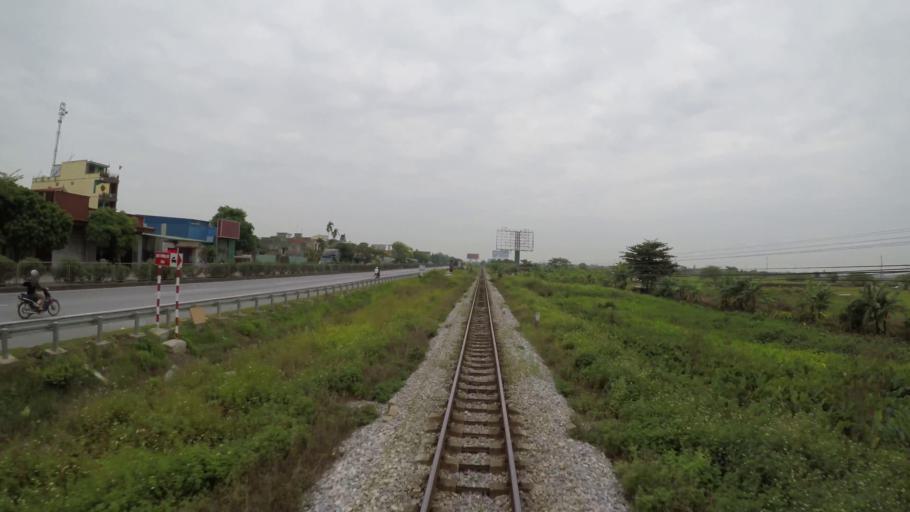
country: VN
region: Hai Duong
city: Phu Thai
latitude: 20.9376
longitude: 106.5484
